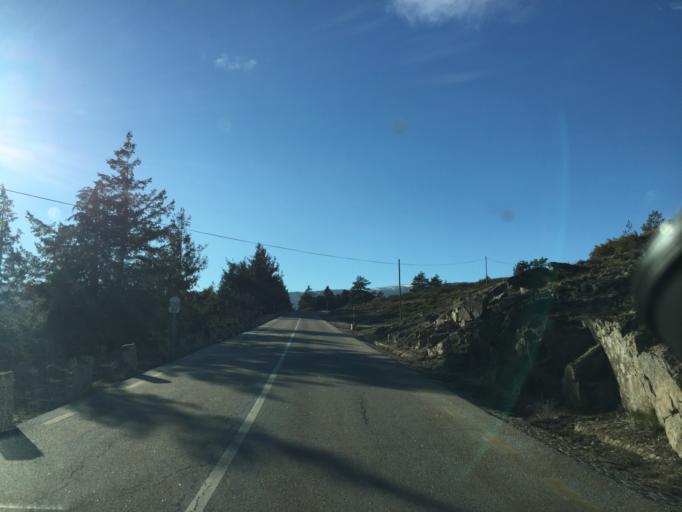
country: PT
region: Castelo Branco
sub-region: Covilha
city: Covilha
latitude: 40.3134
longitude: -7.5556
